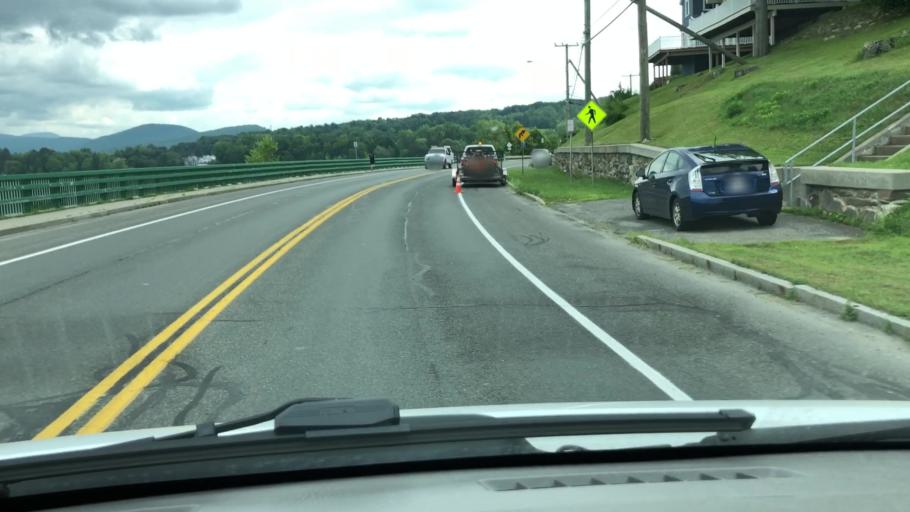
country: US
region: Massachusetts
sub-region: Berkshire County
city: Lanesborough
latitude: 42.4916
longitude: -73.2441
